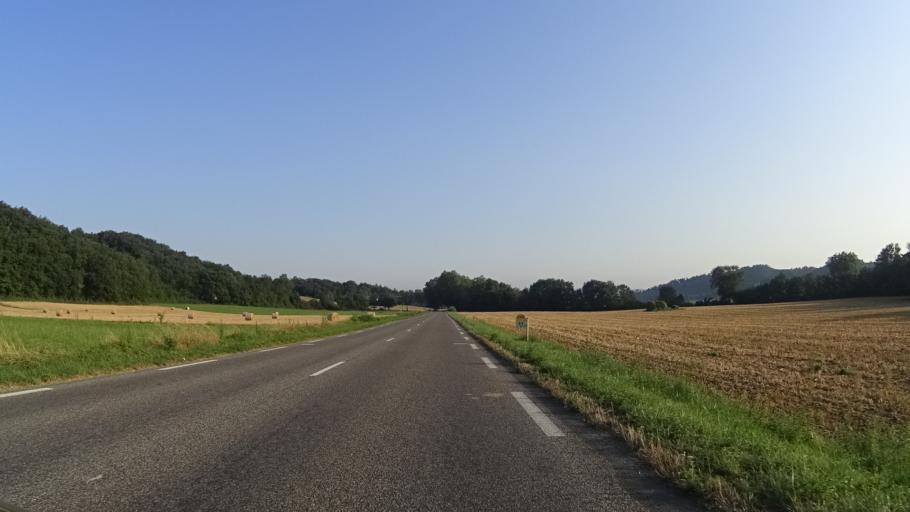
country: FR
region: Midi-Pyrenees
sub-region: Departement de l'Ariege
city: Mirepoix
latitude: 43.0607
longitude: 1.8822
